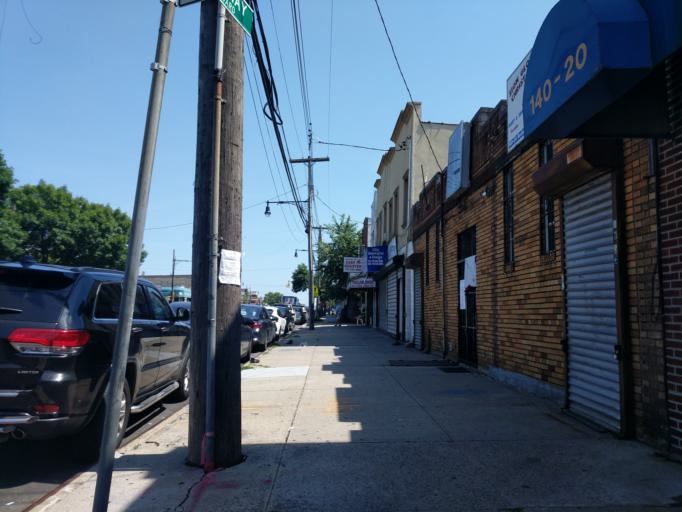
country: US
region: New York
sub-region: Queens County
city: Jamaica
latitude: 40.6741
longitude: -73.8000
